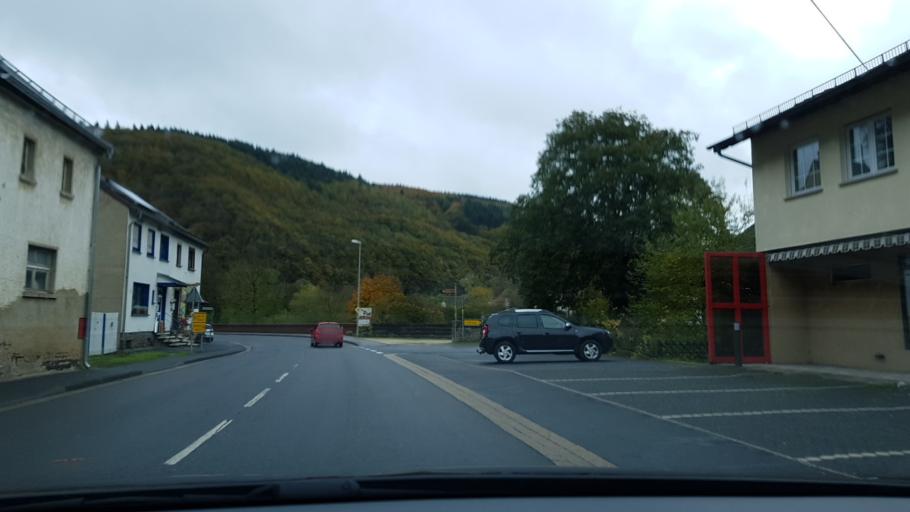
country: DE
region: Rheinland-Pfalz
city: Ahrbruck
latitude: 50.4874
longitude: 6.9718
